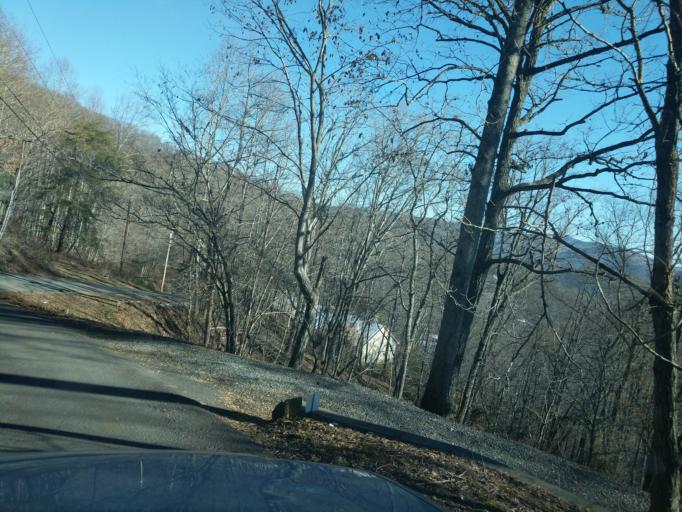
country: US
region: Georgia
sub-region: Towns County
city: Hiawassee
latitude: 34.9495
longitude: -83.7339
